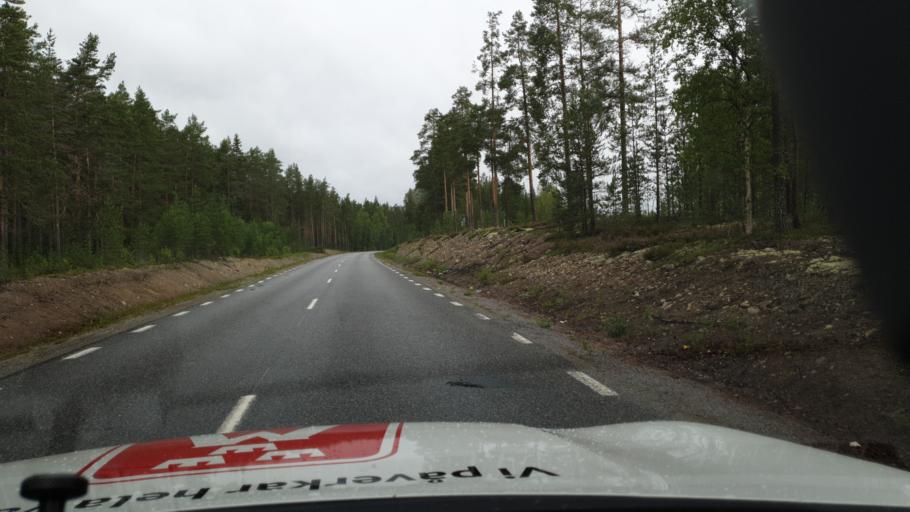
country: SE
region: Vaesterbotten
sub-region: Umea Kommun
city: Saevar
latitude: 63.9455
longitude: 20.5174
